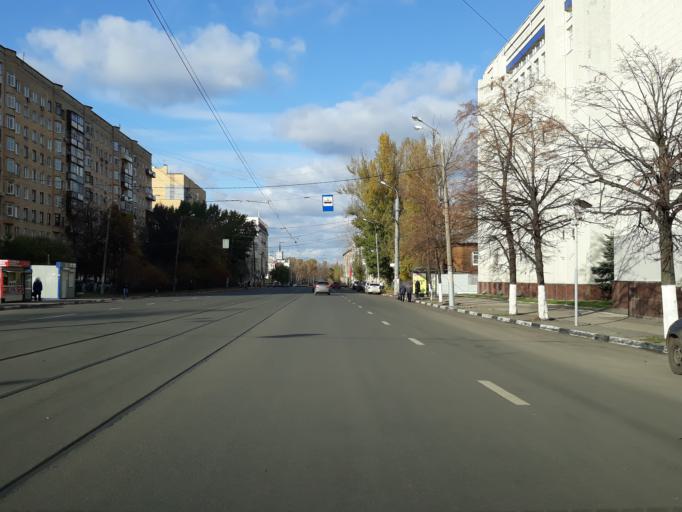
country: RU
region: Nizjnij Novgorod
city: Nizhniy Novgorod
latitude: 56.3018
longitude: 43.9394
